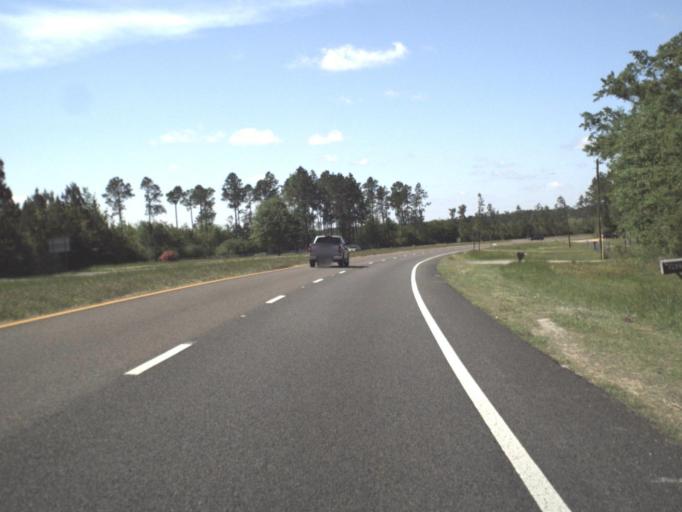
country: US
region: Florida
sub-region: Escambia County
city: Cantonment
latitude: 30.6485
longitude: -87.3502
